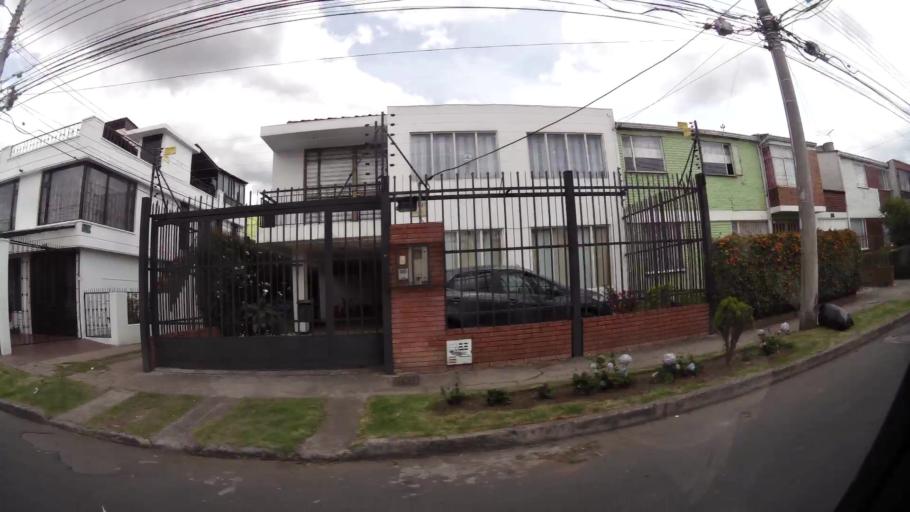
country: CO
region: Cundinamarca
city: Funza
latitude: 4.6977
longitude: -74.1197
